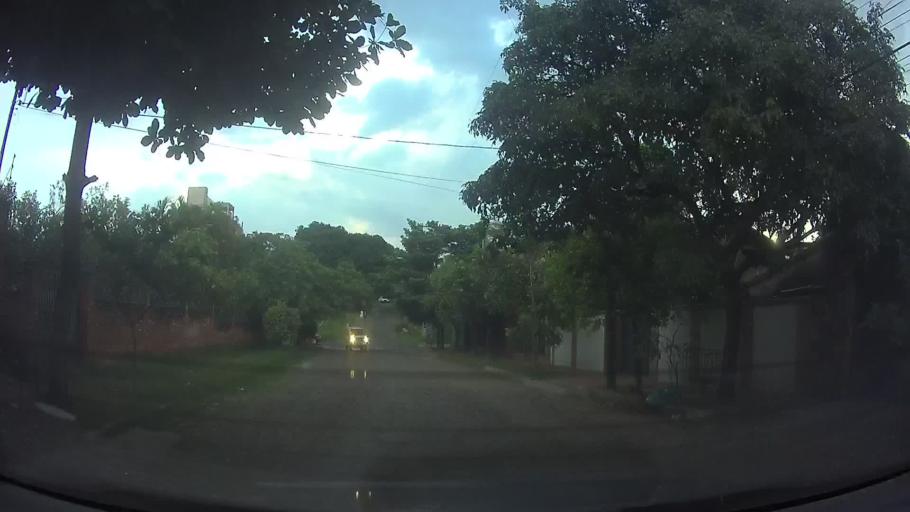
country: PY
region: Asuncion
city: Asuncion
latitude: -25.2679
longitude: -57.5738
